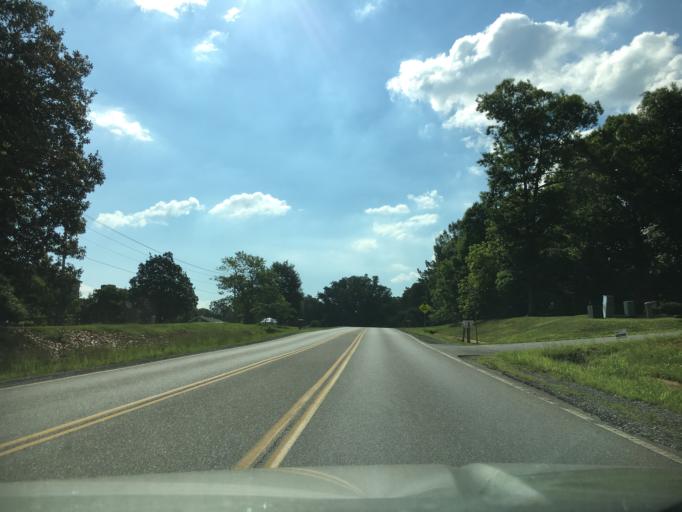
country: US
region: Virginia
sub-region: Bedford County
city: Forest
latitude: 37.3963
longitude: -79.2515
